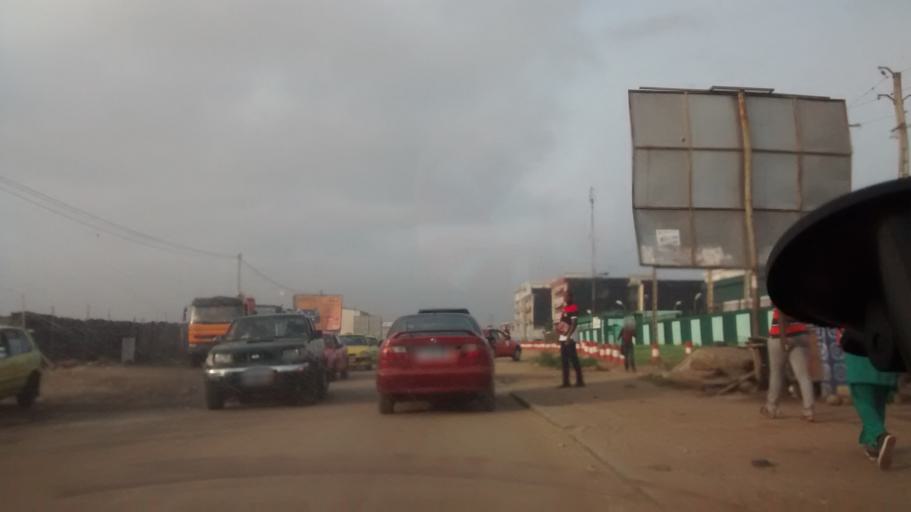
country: CI
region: Lagunes
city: Abobo
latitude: 5.4125
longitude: -3.9814
